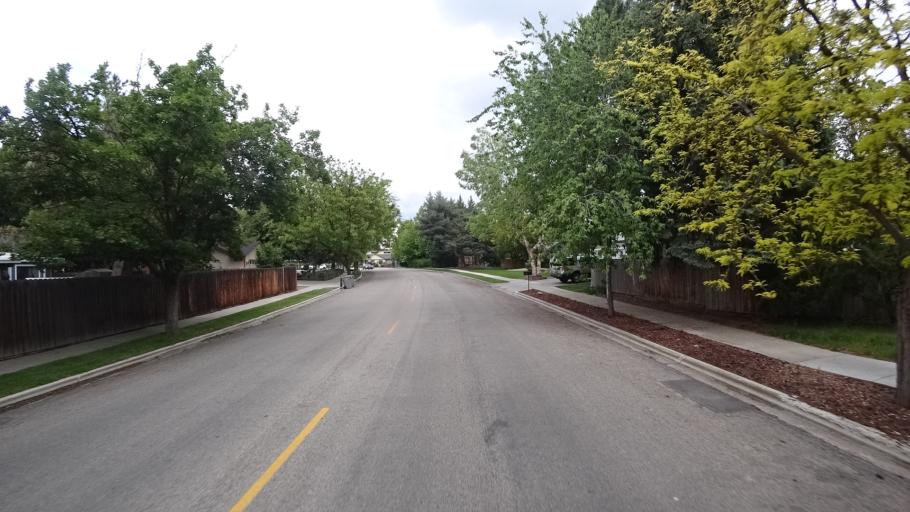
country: US
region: Idaho
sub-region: Ada County
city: Garden City
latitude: 43.6598
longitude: -116.2507
